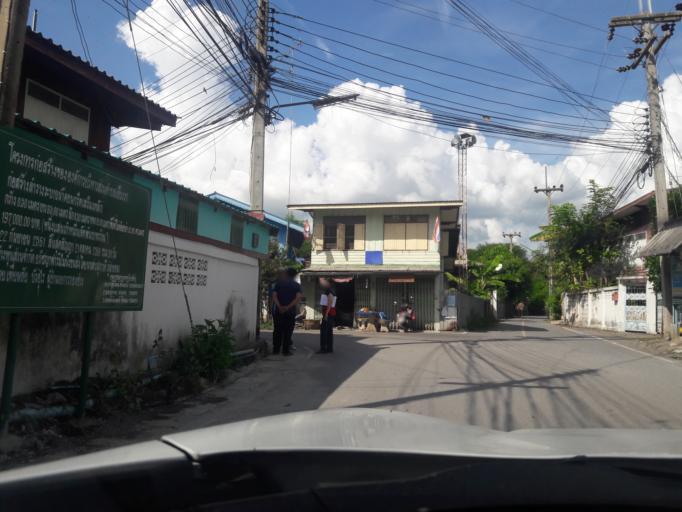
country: TH
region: Lop Buri
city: Ban Mi
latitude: 15.0495
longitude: 100.5387
